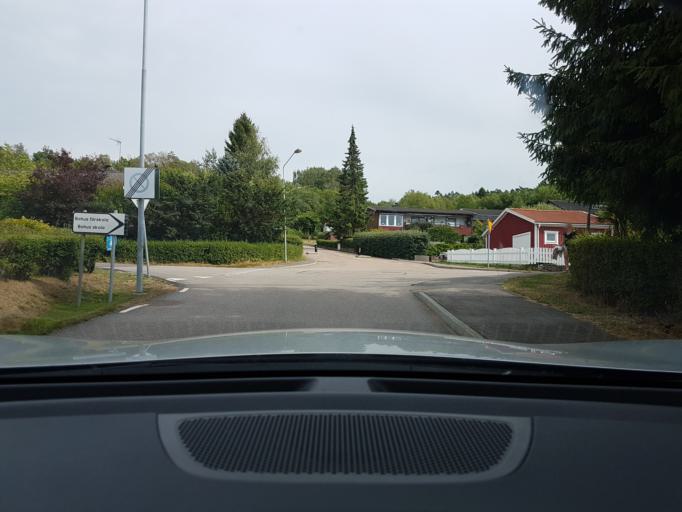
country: SE
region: Vaestra Goetaland
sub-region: Ale Kommun
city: Surte
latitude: 57.8496
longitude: 12.0231
